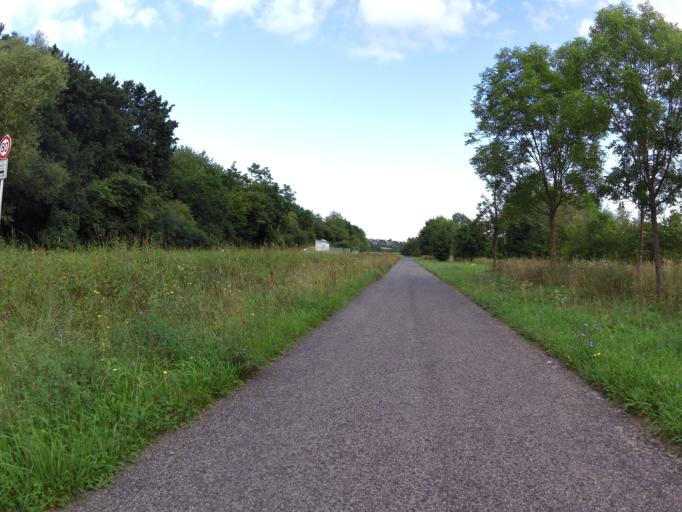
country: DE
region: Bavaria
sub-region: Regierungsbezirk Unterfranken
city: Kitzingen
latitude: 49.7530
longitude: 10.1556
